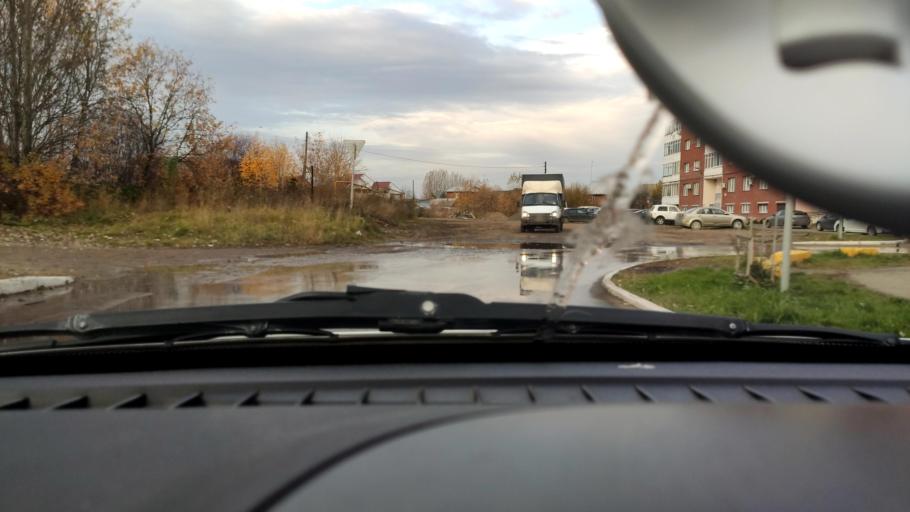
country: RU
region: Perm
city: Kondratovo
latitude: 57.9743
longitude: 56.1031
